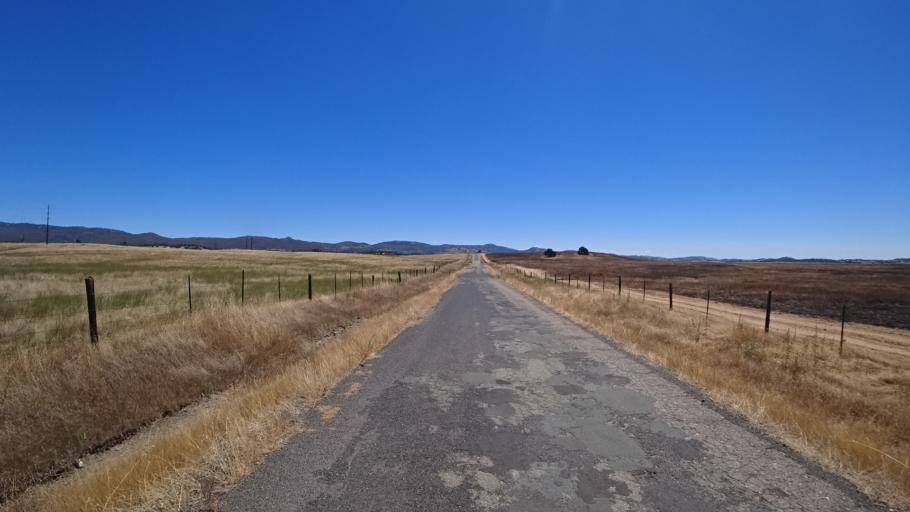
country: US
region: California
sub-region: Calaveras County
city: Rancho Calaveras
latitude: 38.0573
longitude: -120.7669
